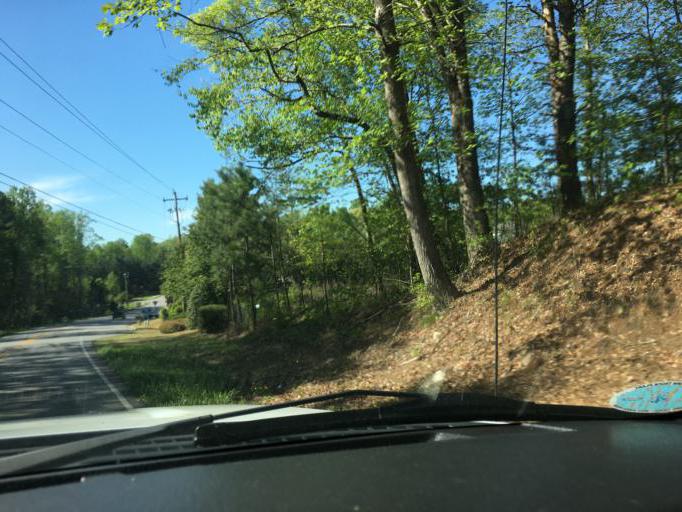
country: US
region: Georgia
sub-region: Forsyth County
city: Cumming
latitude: 34.3064
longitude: -84.1616
